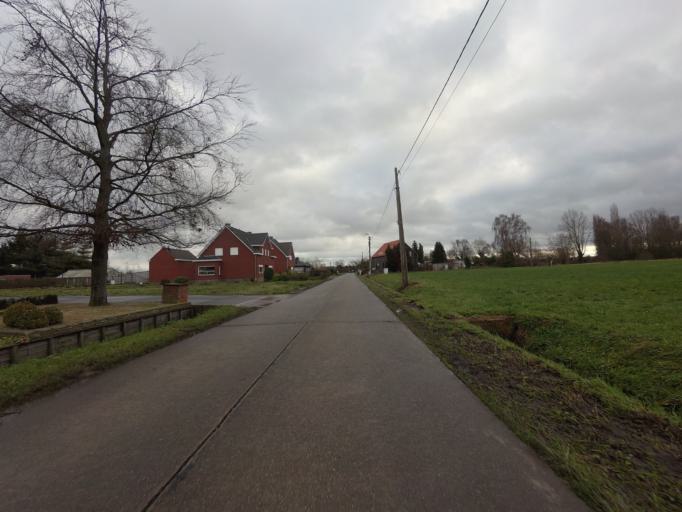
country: BE
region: Flanders
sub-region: Provincie Antwerpen
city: Sint-Katelijne-Waver
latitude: 51.0995
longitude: 4.5430
